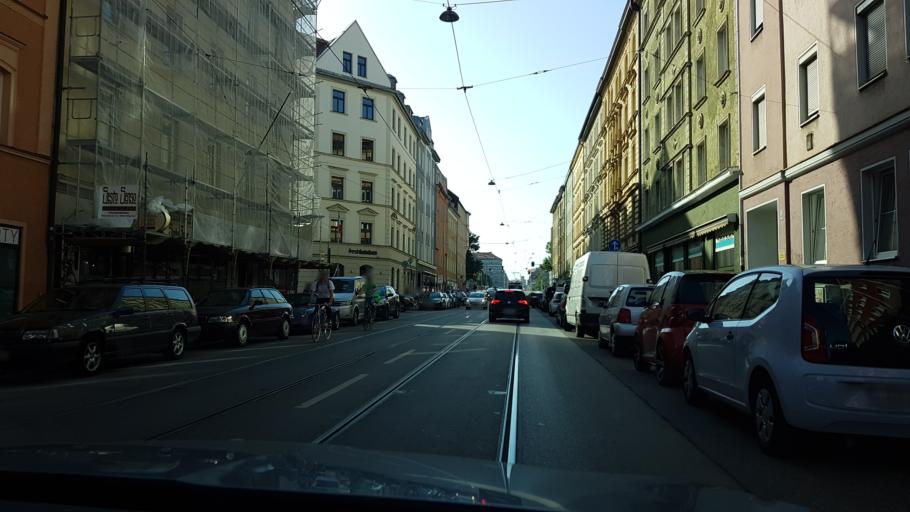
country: DE
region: Bavaria
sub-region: Upper Bavaria
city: Munich
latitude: 48.1255
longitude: 11.5795
